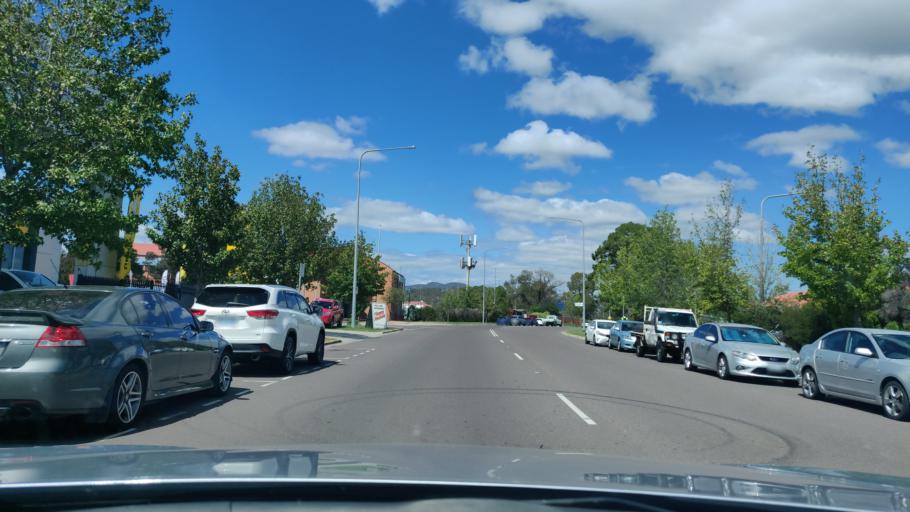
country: AU
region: Australian Capital Territory
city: Macarthur
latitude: -35.4227
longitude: 149.0699
